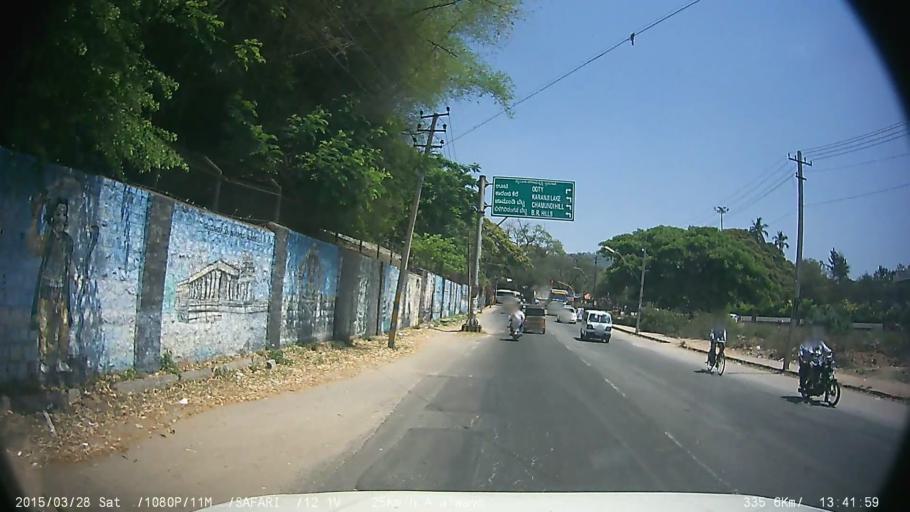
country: IN
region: Karnataka
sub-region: Mysore
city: Mysore
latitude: 12.2992
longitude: 76.6660
